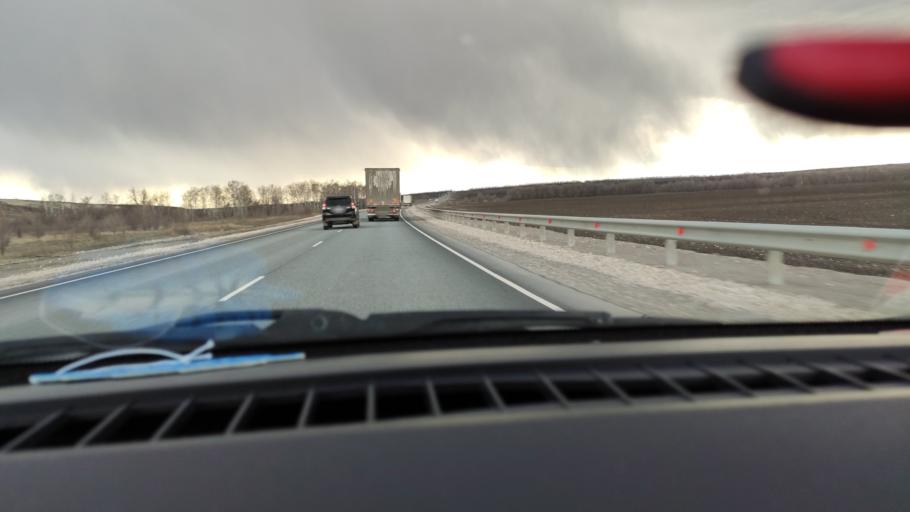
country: RU
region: Saratov
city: Yelshanka
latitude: 51.8539
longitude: 46.4919
